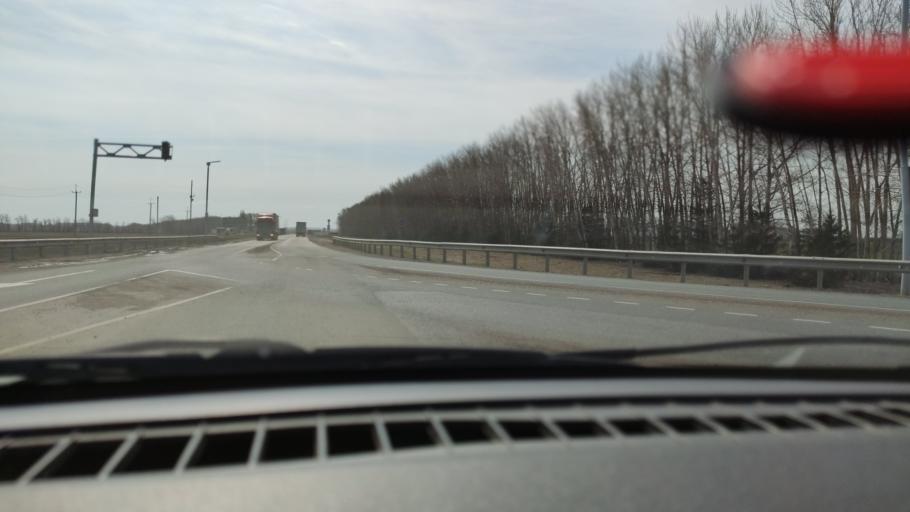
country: RU
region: Bashkortostan
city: Dyurtyuli
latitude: 55.4245
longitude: 54.8074
